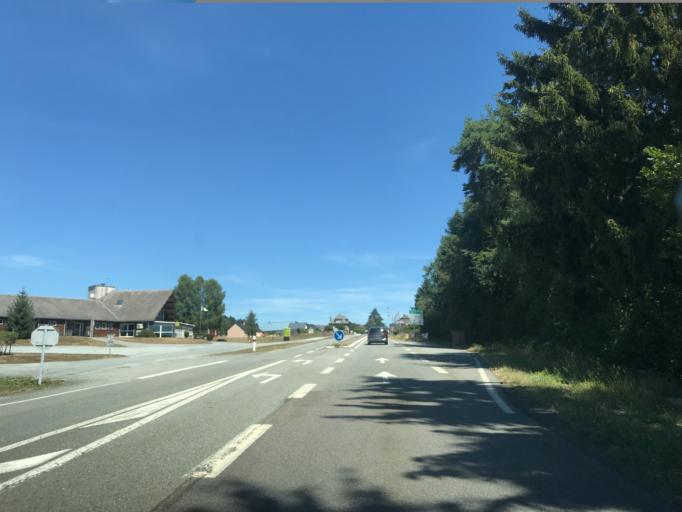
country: FR
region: Limousin
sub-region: Departement de la Correze
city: Meymac
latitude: 45.4649
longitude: 2.1409
